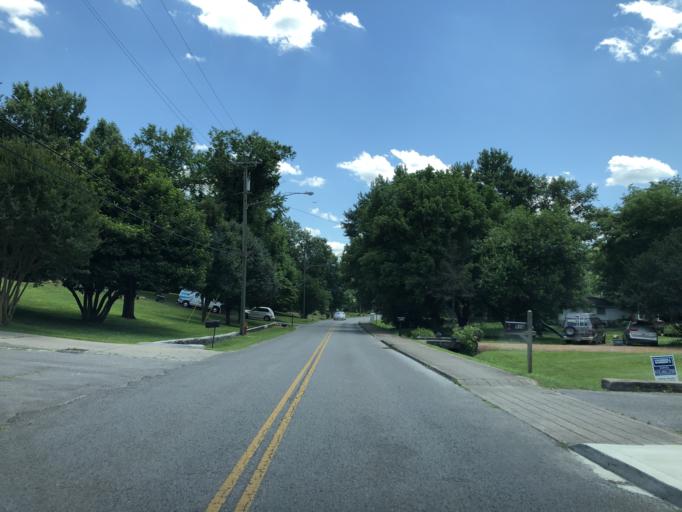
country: US
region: Tennessee
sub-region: Davidson County
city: Nashville
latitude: 36.1823
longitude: -86.7177
